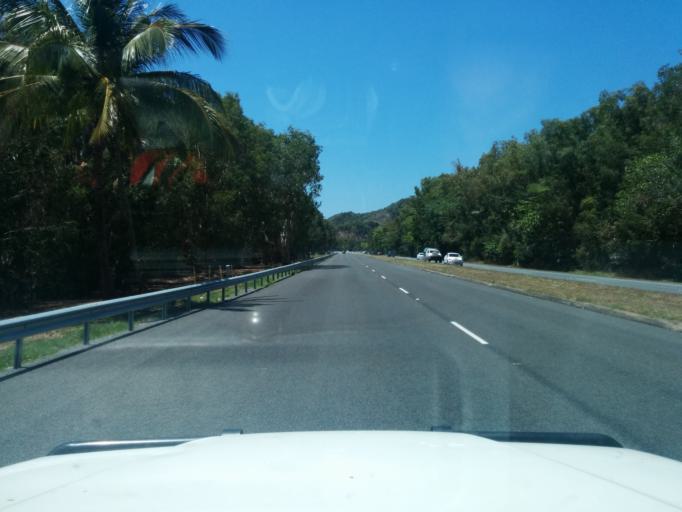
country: AU
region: Queensland
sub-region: Cairns
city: Redlynch
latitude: -16.8786
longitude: 145.7447
